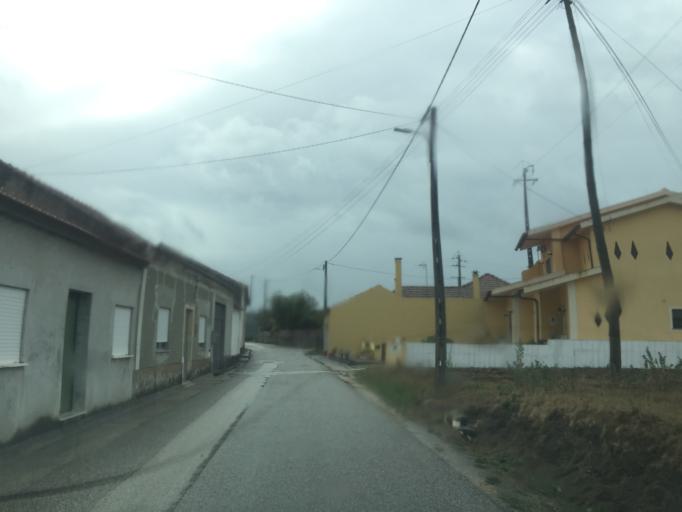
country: PT
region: Coimbra
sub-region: Figueira da Foz
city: Lavos
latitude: 40.0613
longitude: -8.7712
